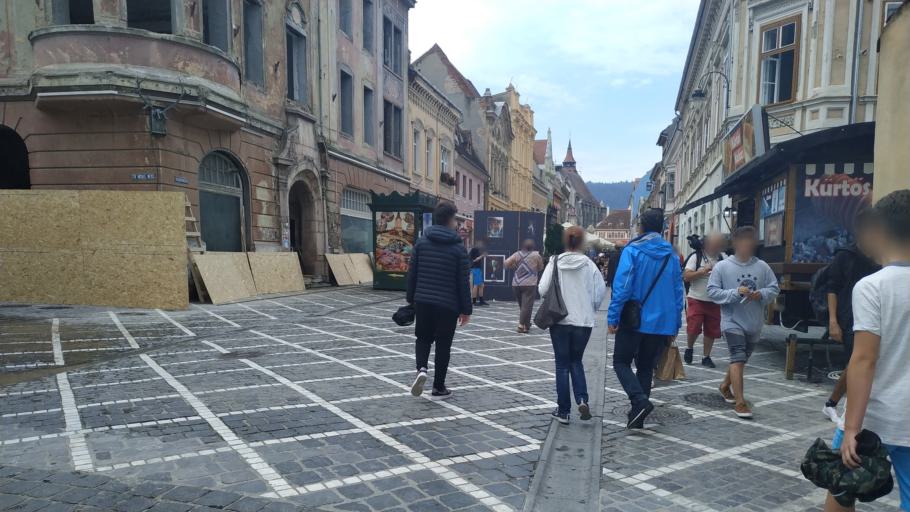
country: RO
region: Brasov
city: Brasov
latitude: 45.6430
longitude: 25.5918
